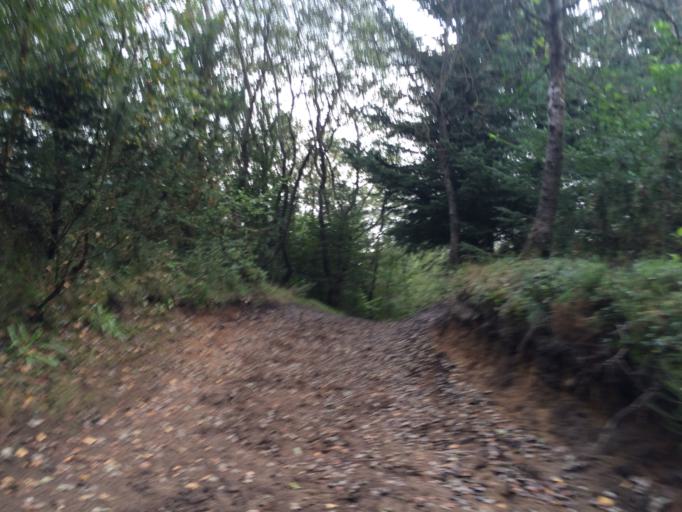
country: DK
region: Central Jutland
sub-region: Holstebro Kommune
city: Ulfborg
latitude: 56.2367
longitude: 8.4150
